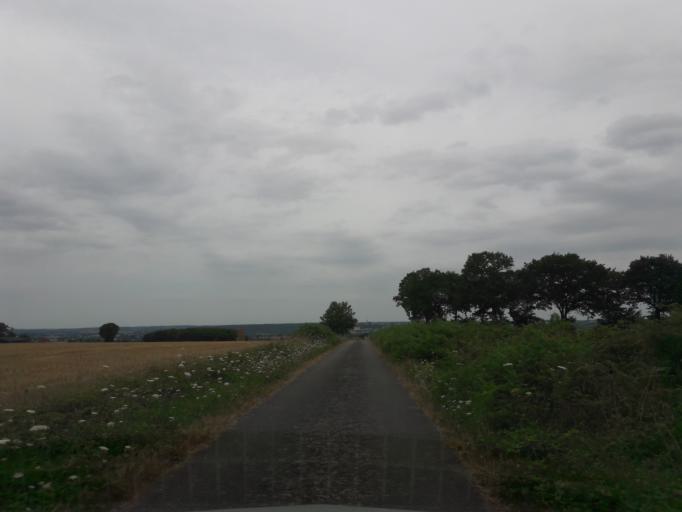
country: FR
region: Brittany
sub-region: Departement d'Ille-et-Vilaine
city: Bain-de-Bretagne
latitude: 47.8409
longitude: -1.6645
